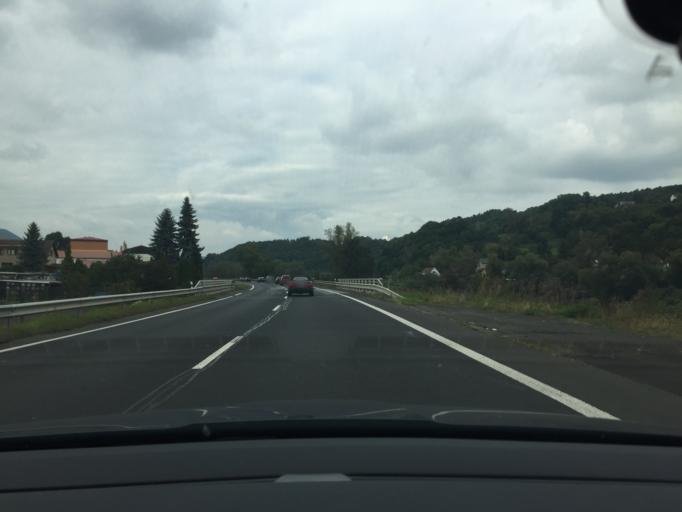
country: CZ
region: Ustecky
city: Povrly
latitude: 50.7117
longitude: 14.1952
